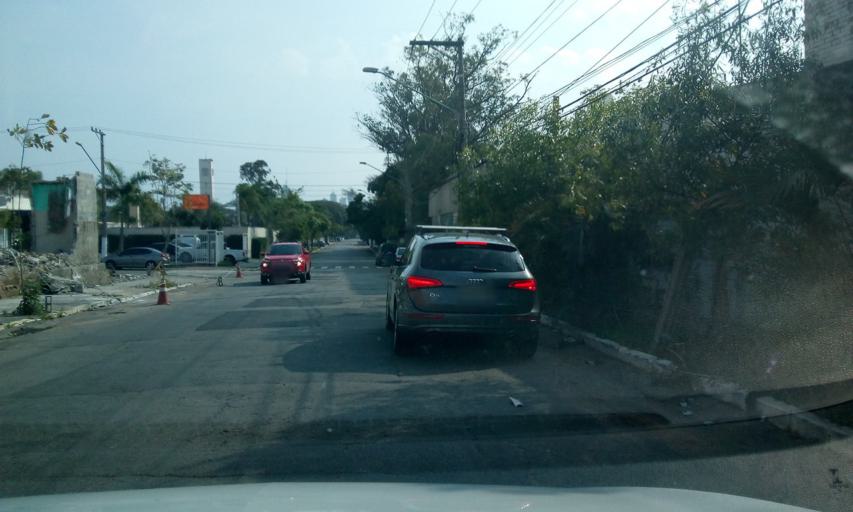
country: BR
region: Sao Paulo
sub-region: Osasco
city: Osasco
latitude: -23.5314
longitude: -46.7323
